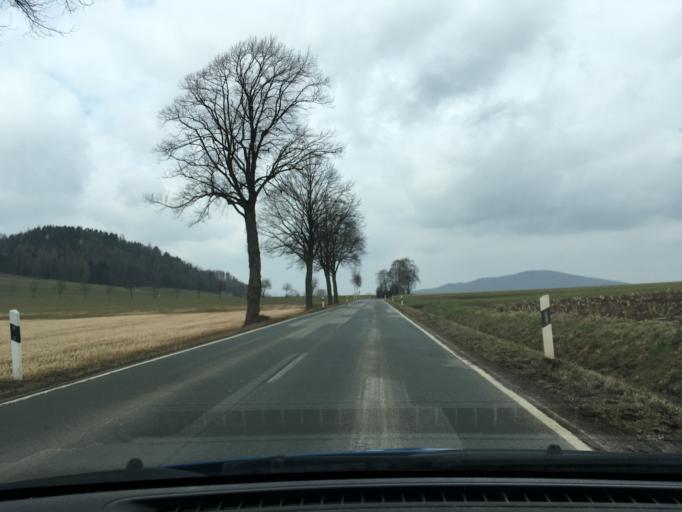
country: DE
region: Lower Saxony
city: Dransfeld
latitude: 51.5259
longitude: 9.7290
